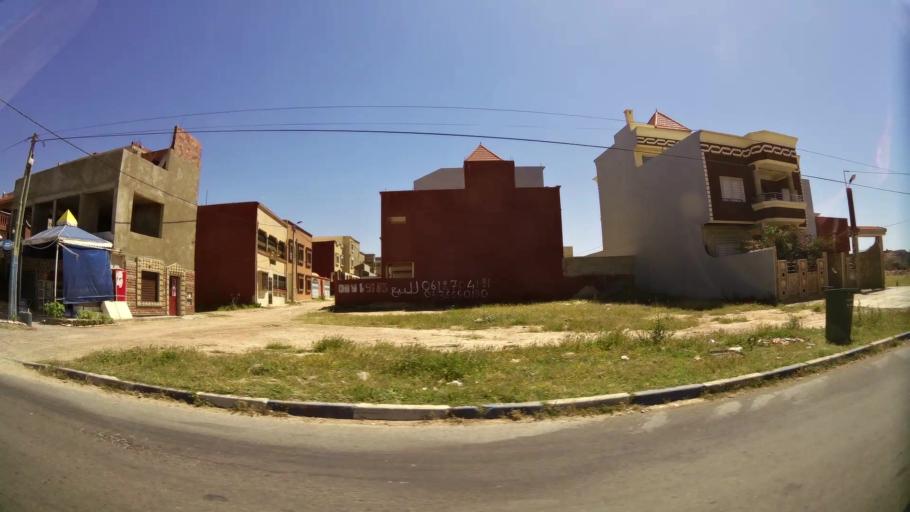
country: MA
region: Oriental
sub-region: Berkane-Taourirt
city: Madagh
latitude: 35.1349
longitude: -2.4079
